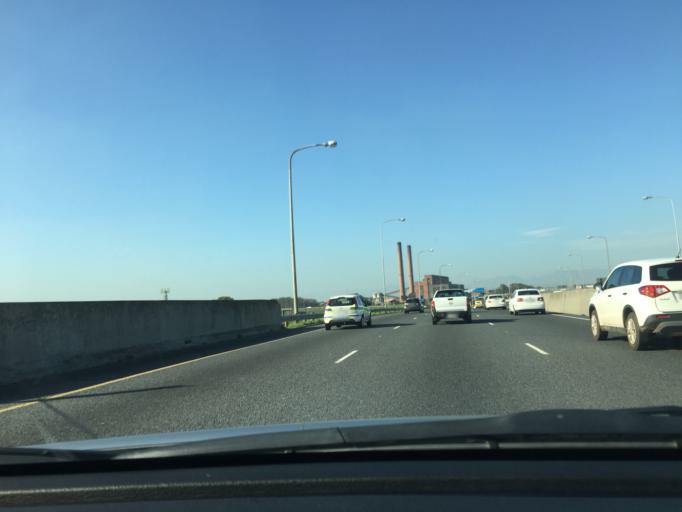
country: ZA
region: Western Cape
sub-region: City of Cape Town
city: Rosebank
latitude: -33.9498
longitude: 18.5024
